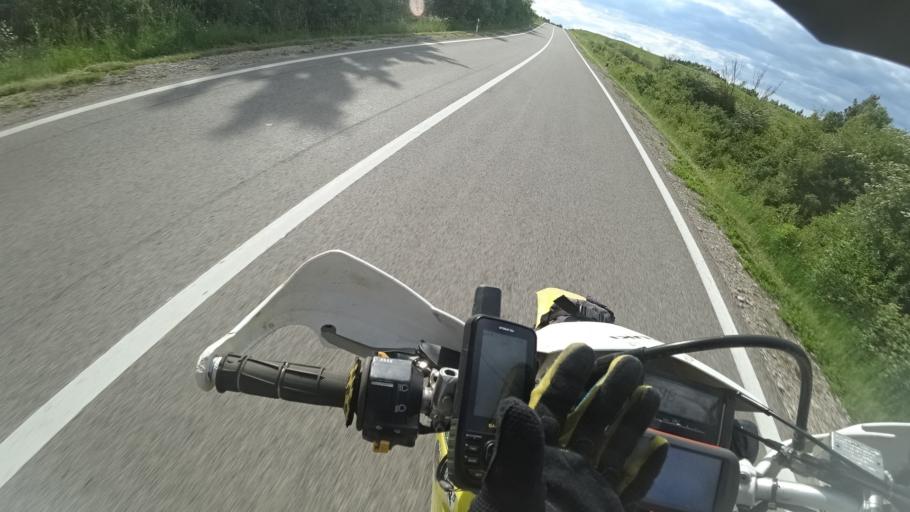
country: HR
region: Licko-Senjska
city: Gospic
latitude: 44.5020
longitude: 15.4505
